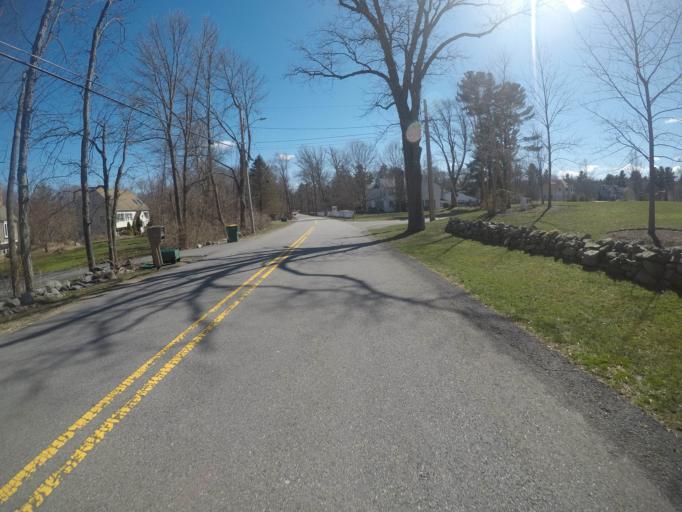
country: US
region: Massachusetts
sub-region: Bristol County
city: Easton
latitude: 41.9986
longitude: -71.1003
